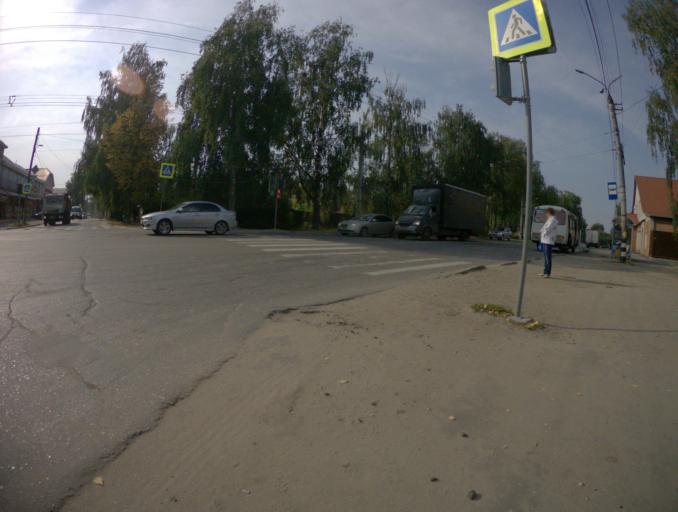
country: RU
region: Vladimir
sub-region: Kovrovskiy Rayon
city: Kovrov
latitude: 56.3630
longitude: 41.3057
